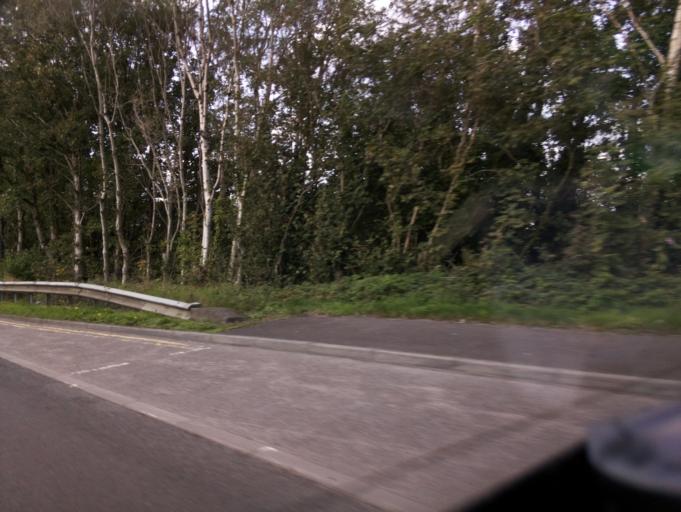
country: GB
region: Wales
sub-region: Rhondda Cynon Taf
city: Llantrisant
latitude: 51.5315
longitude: -3.3711
